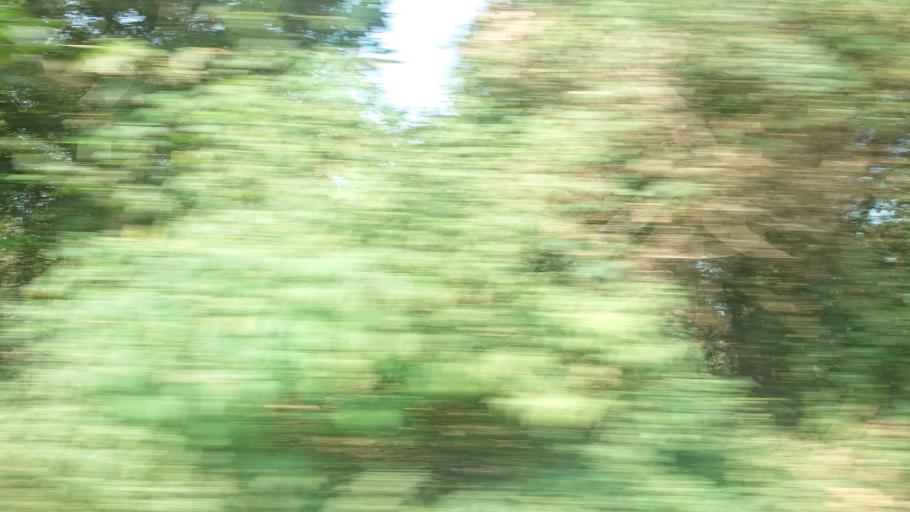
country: TW
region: Taiwan
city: Lugu
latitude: 23.7154
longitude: 120.6683
